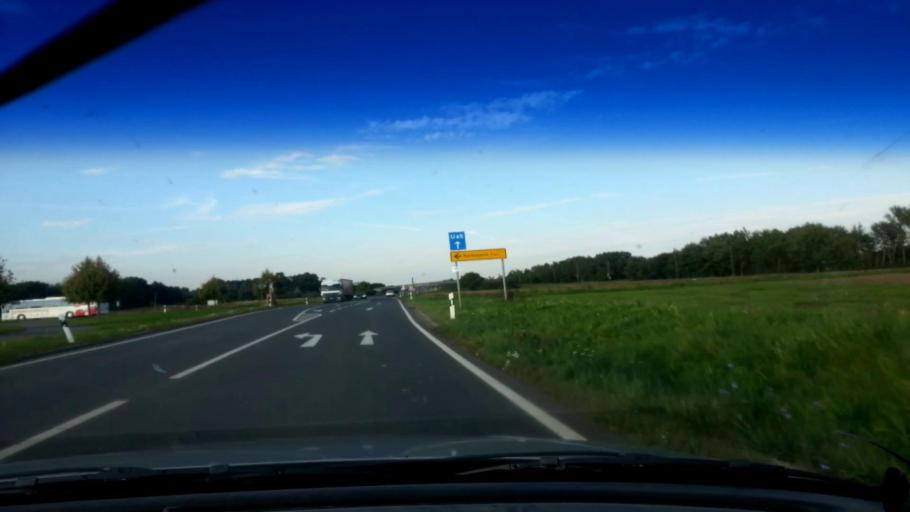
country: DE
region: Bavaria
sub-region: Upper Franconia
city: Kemmern
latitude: 49.9482
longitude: 10.8851
